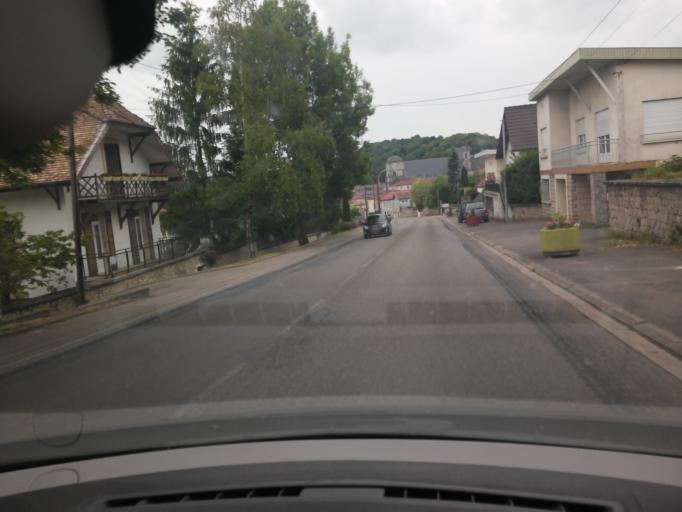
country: FR
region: Lorraine
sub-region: Departement de la Meuse
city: Saint-Mihiel
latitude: 48.8860
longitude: 5.5373
